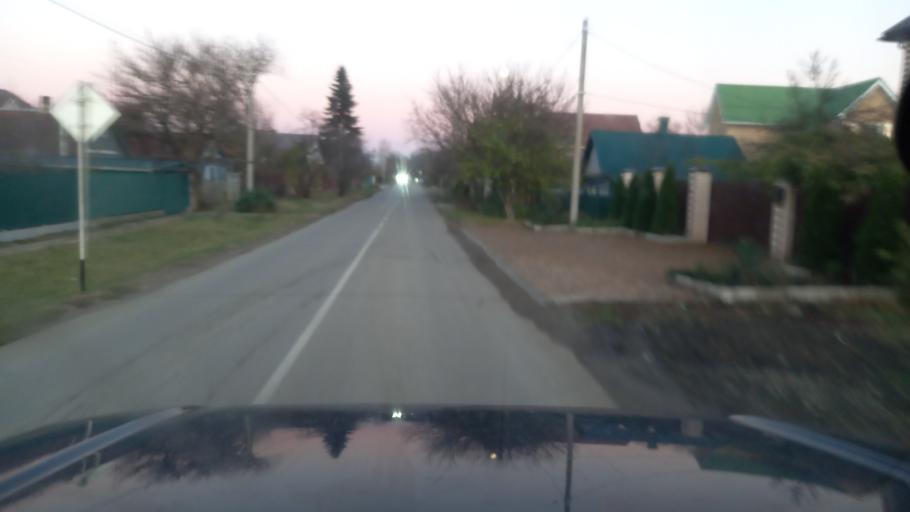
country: RU
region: Krasnodarskiy
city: Goryachiy Klyuch
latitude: 44.6322
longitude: 39.1124
